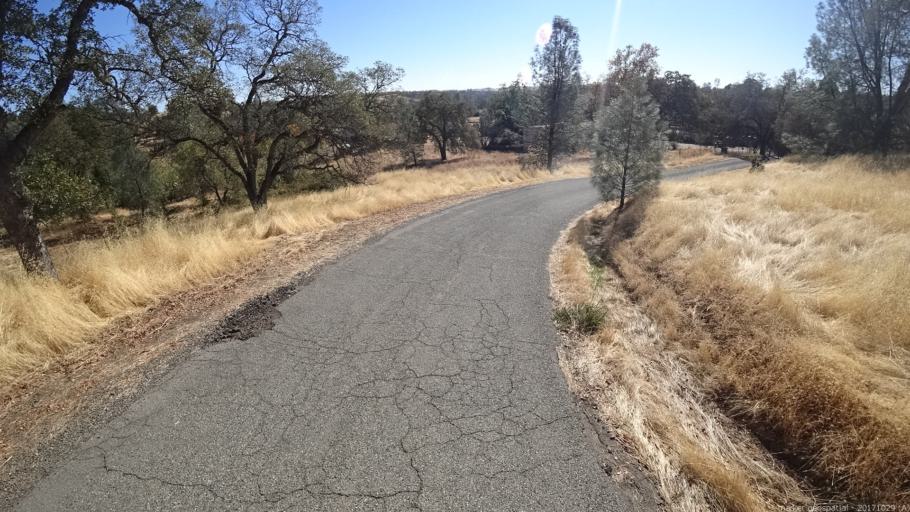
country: US
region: California
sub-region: Shasta County
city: Shasta
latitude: 40.4757
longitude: -122.6194
